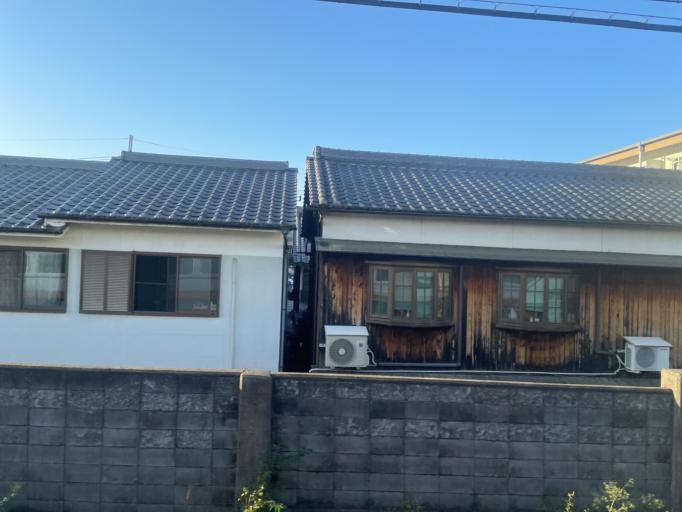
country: JP
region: Nara
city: Kashihara-shi
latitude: 34.5129
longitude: 135.7948
